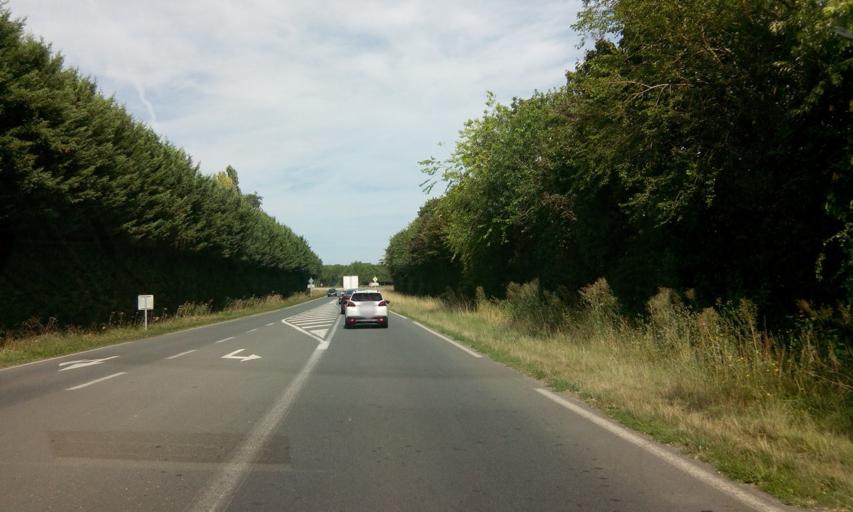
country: FR
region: Poitou-Charentes
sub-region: Departement des Deux-Sevres
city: Sauze-Vaussais
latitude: 46.1347
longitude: 0.1113
